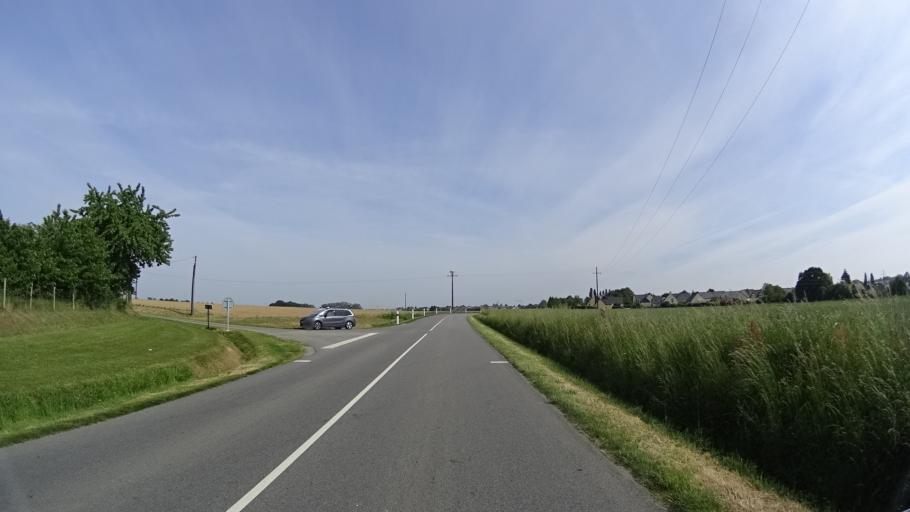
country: FR
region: Brittany
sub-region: Departement d'Ille-et-Vilaine
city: Chateaugiron
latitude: 48.0294
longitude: -1.5051
